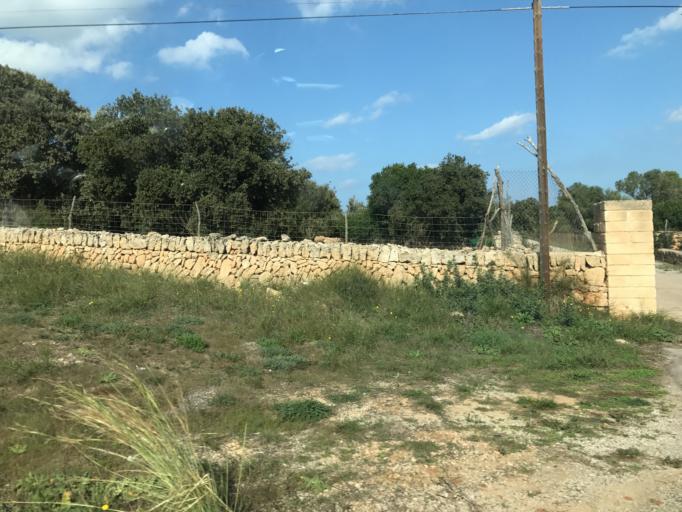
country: ES
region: Balearic Islands
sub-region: Illes Balears
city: Santa Margalida
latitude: 39.7278
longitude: 3.1980
